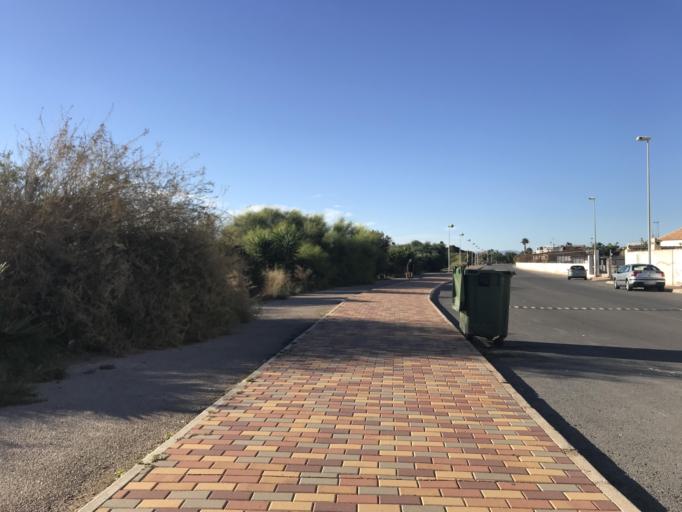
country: ES
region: Valencia
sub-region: Provincia de Alicante
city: Torrevieja
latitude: 37.9817
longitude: -0.6958
